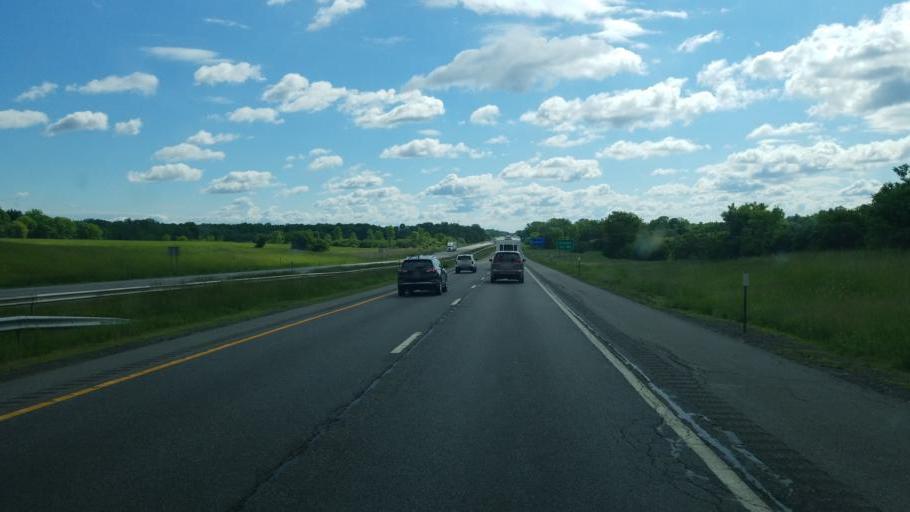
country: US
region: New York
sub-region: Cayuga County
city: Centerport
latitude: 43.0569
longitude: -76.5851
